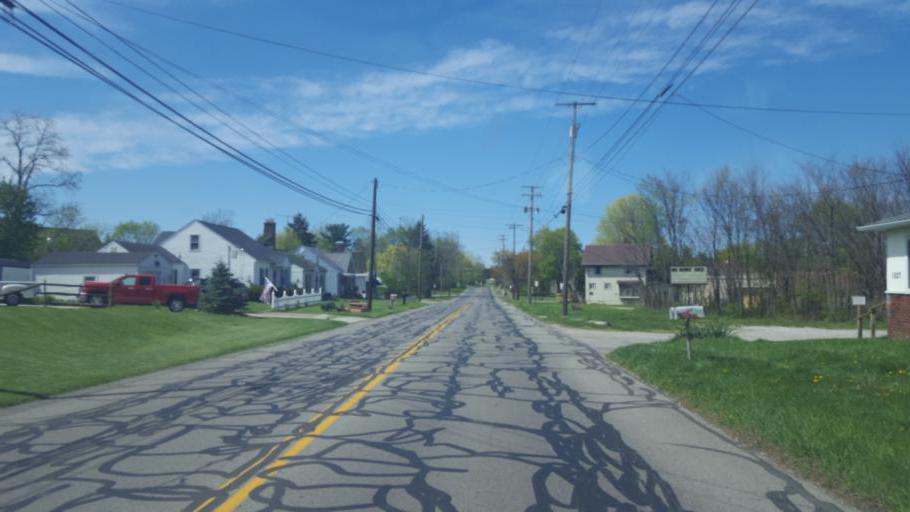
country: US
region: Ohio
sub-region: Ashland County
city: Ashland
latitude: 40.8809
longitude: -82.3214
